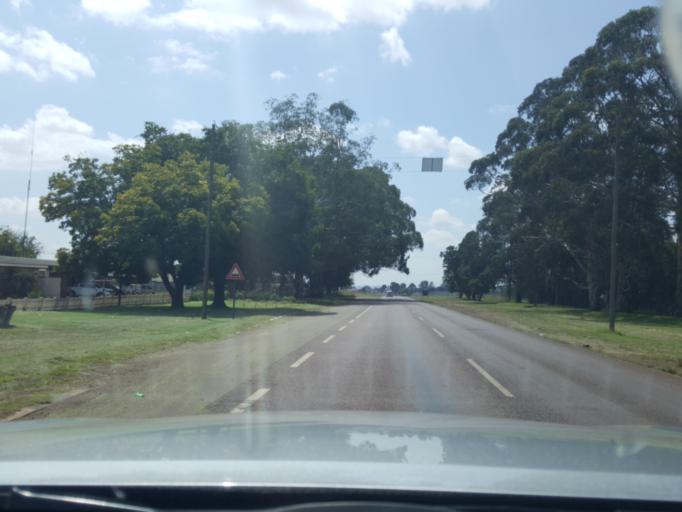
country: ZA
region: Mpumalanga
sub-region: Nkangala District Municipality
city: Middelburg
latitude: -25.9810
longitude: 29.4522
